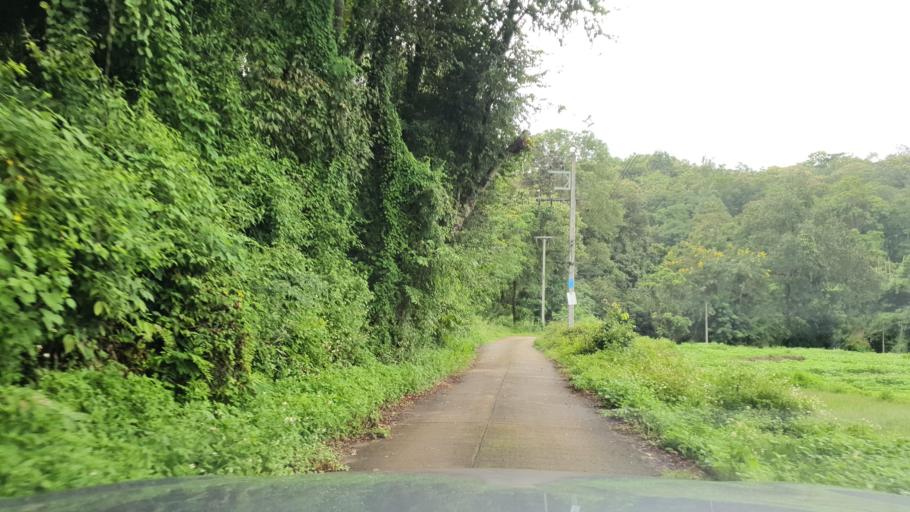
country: TH
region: Chiang Mai
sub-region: Amphoe Chiang Dao
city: Chiang Dao
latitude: 19.3382
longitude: 98.9265
